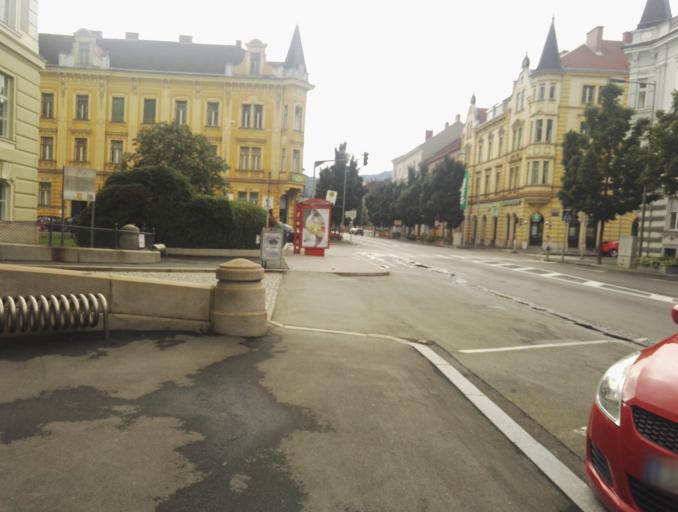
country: AT
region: Styria
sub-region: Politischer Bezirk Leoben
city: Leoben
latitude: 47.3846
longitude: 15.0928
